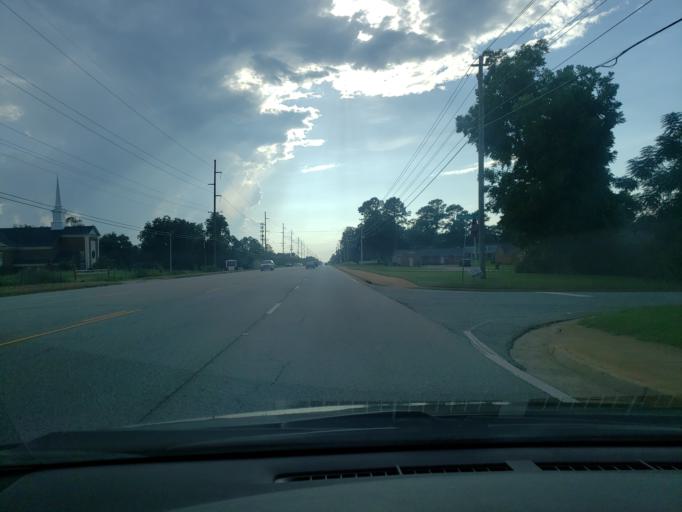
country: US
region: Georgia
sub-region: Dougherty County
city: Albany
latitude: 31.5857
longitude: -84.2290
